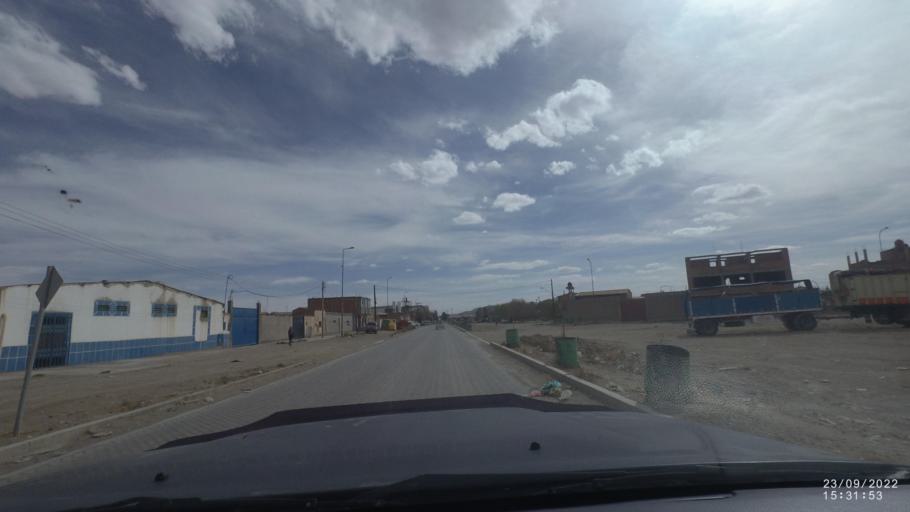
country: BO
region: Oruro
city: Oruro
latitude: -17.9749
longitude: -67.0555
